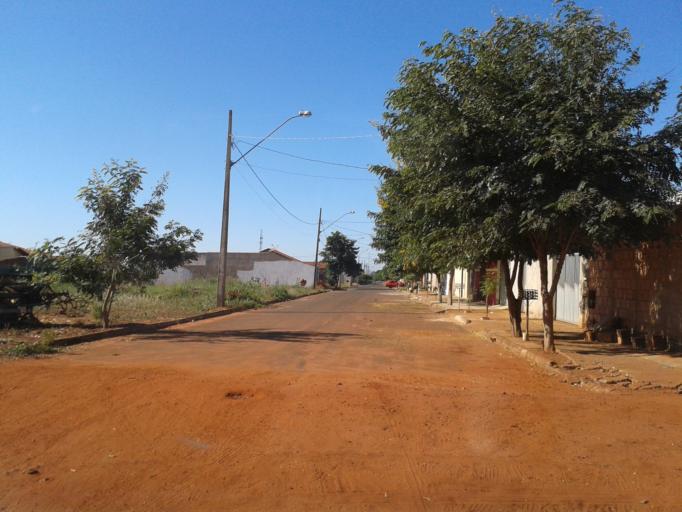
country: BR
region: Minas Gerais
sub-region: Santa Vitoria
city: Santa Vitoria
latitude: -18.8595
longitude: -50.1279
